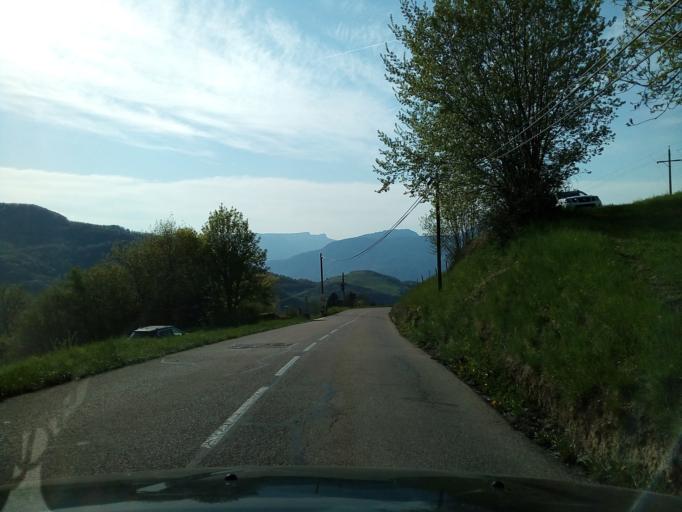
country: FR
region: Rhone-Alpes
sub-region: Departement de l'Isere
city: Revel
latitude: 45.1828
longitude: 5.8775
